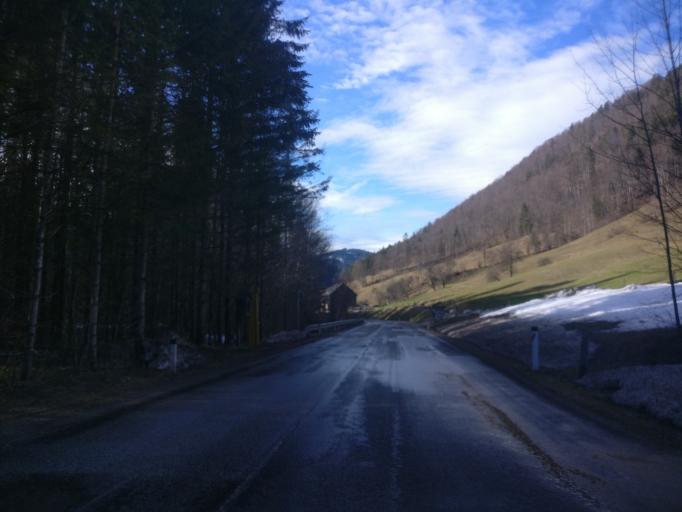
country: AT
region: Styria
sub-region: Politischer Bezirk Liezen
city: Altenmarkt bei Sankt Gallen
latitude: 47.6760
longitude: 14.6408
